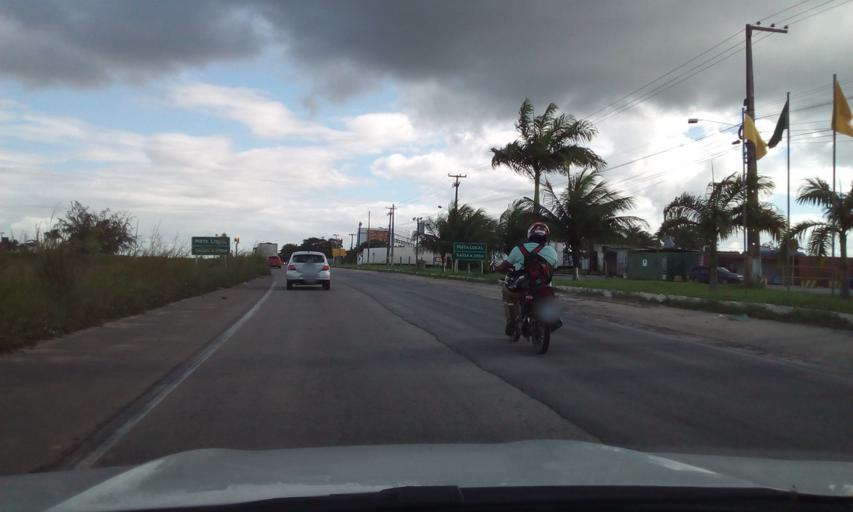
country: BR
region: Pernambuco
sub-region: Paulista
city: Paulista
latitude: -7.9630
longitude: -34.9153
